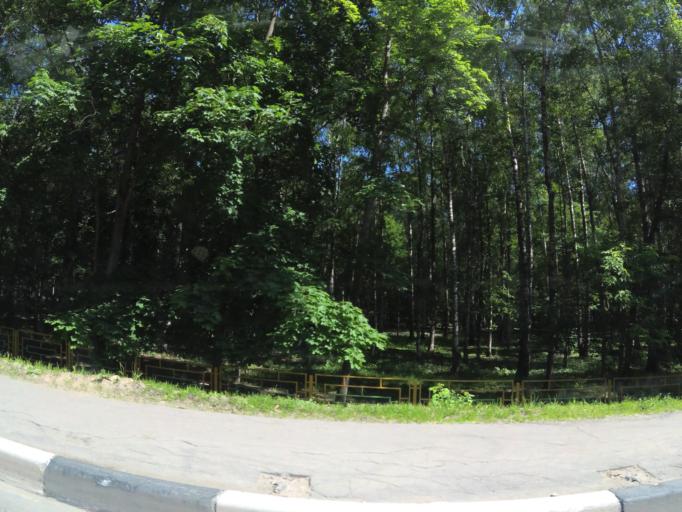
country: RU
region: Moskovskaya
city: Lobnya
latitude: 56.0116
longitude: 37.4680
